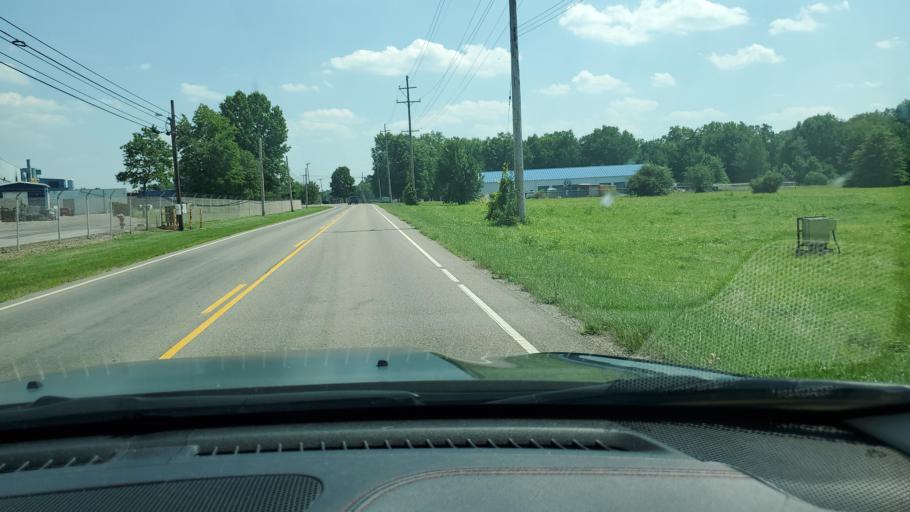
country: US
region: Ohio
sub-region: Trumbull County
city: Bolindale
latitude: 41.1890
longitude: -80.7848
